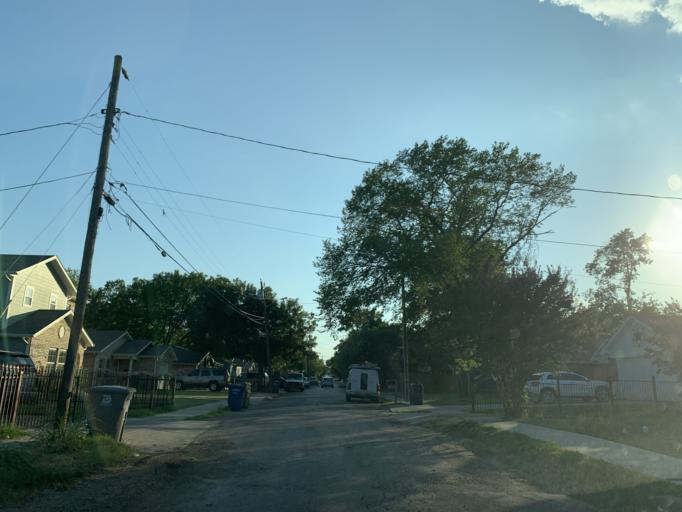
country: US
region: Texas
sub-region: Dallas County
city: Dallas
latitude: 32.7058
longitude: -96.7817
